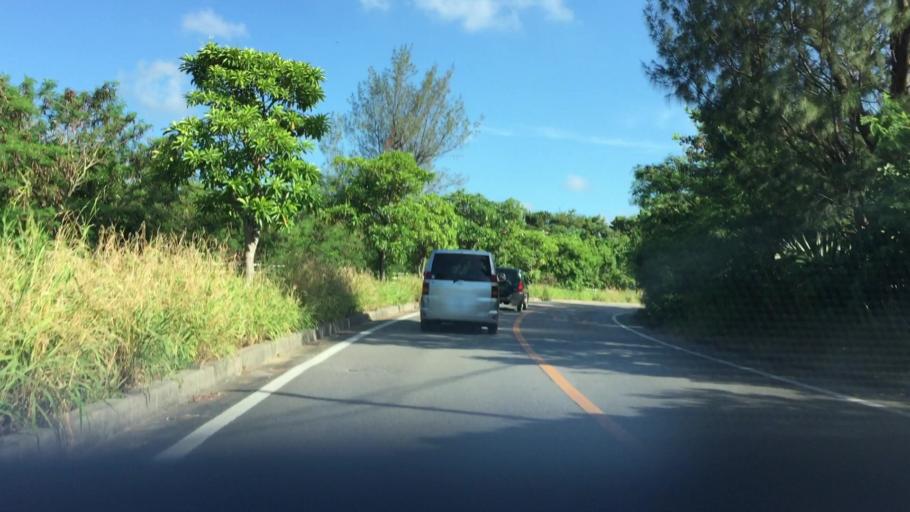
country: JP
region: Okinawa
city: Ishigaki
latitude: 24.4186
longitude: 124.1344
